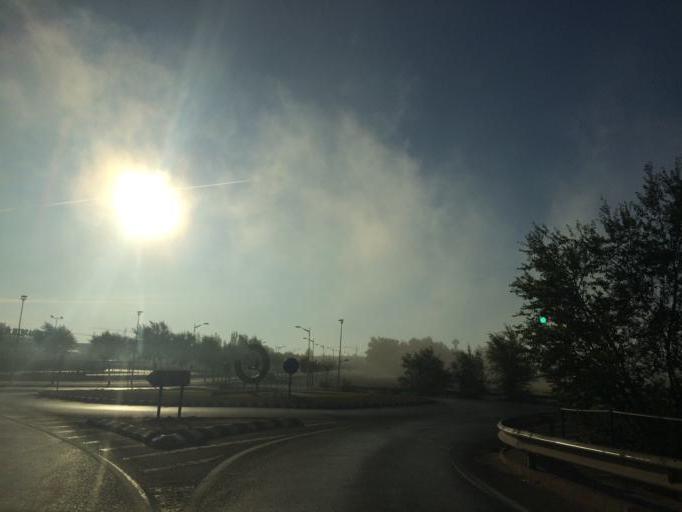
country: ES
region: Castille-La Mancha
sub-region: Provincia de Albacete
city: Albacete
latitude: 39.0063
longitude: -1.8870
